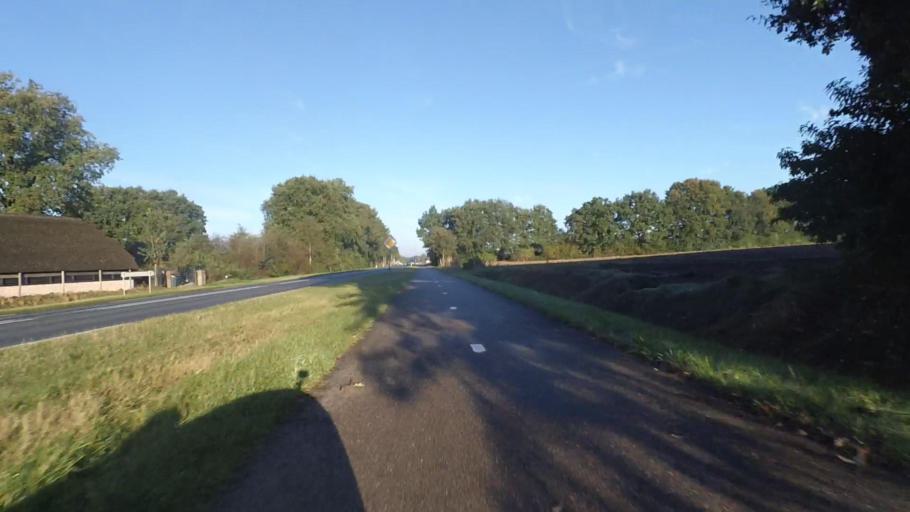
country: NL
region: Gelderland
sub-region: Gemeente Apeldoorn
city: Uddel
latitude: 52.2352
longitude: 5.7696
